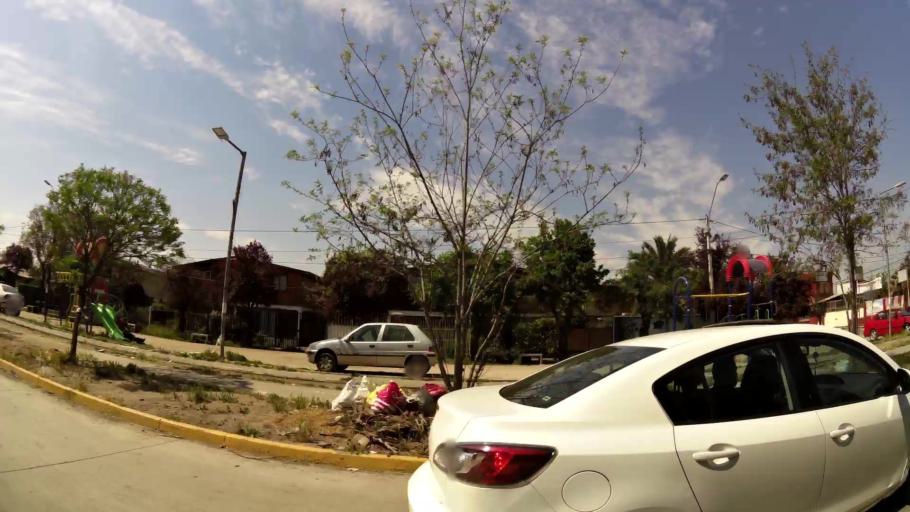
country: CL
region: Santiago Metropolitan
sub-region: Provincia de Santiago
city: La Pintana
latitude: -33.5449
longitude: -70.6663
